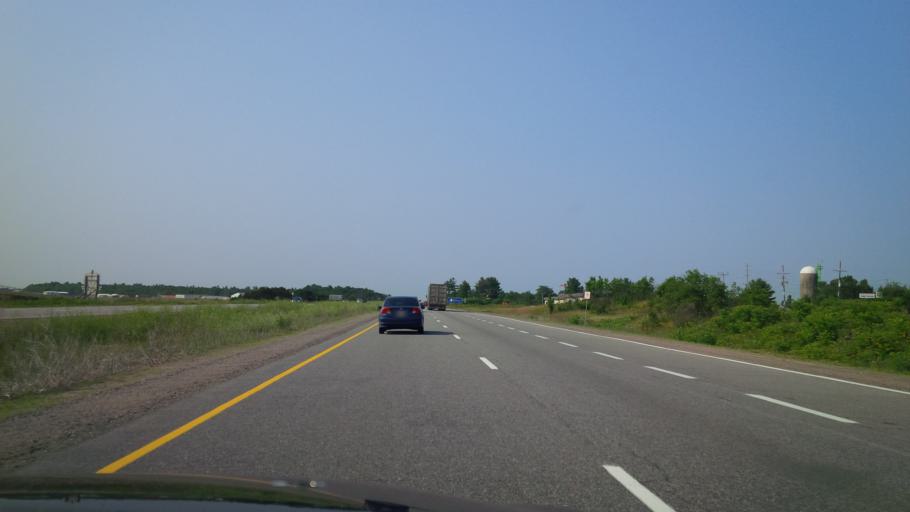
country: CA
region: Ontario
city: Bracebridge
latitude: 44.9911
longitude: -79.3088
